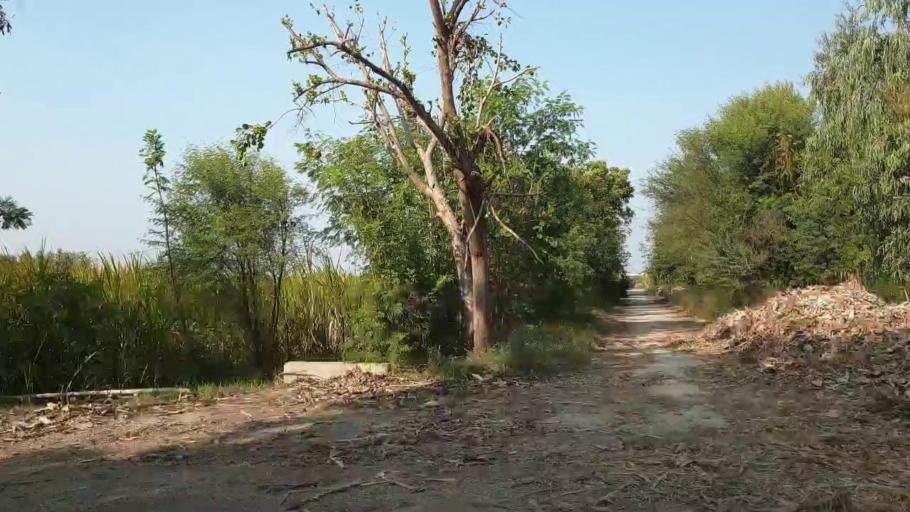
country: PK
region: Sindh
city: Tando Adam
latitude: 25.6617
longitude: 68.5697
